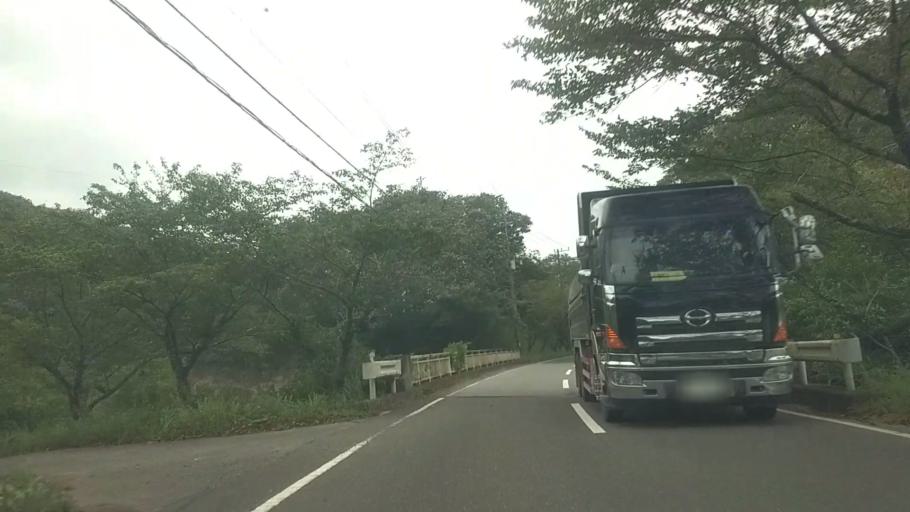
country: JP
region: Chiba
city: Kimitsu
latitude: 35.2258
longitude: 139.9551
